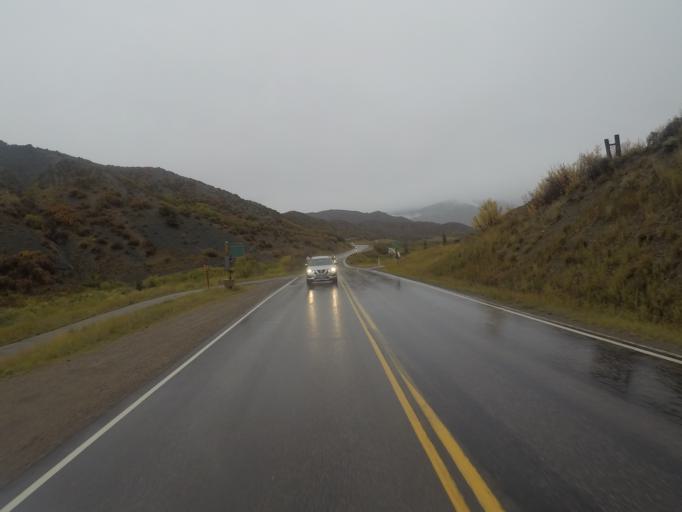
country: US
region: Colorado
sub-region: Pitkin County
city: Snowmass Village
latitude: 39.2278
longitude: -106.9182
